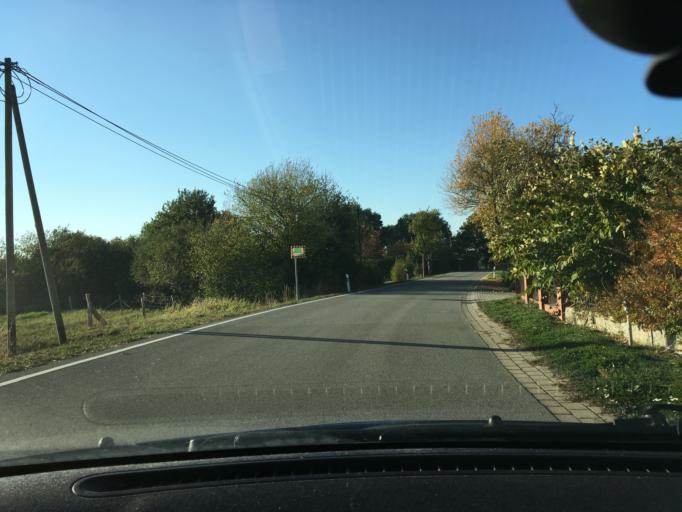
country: DE
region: Lower Saxony
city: Hitzacker
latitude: 53.1851
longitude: 11.0144
